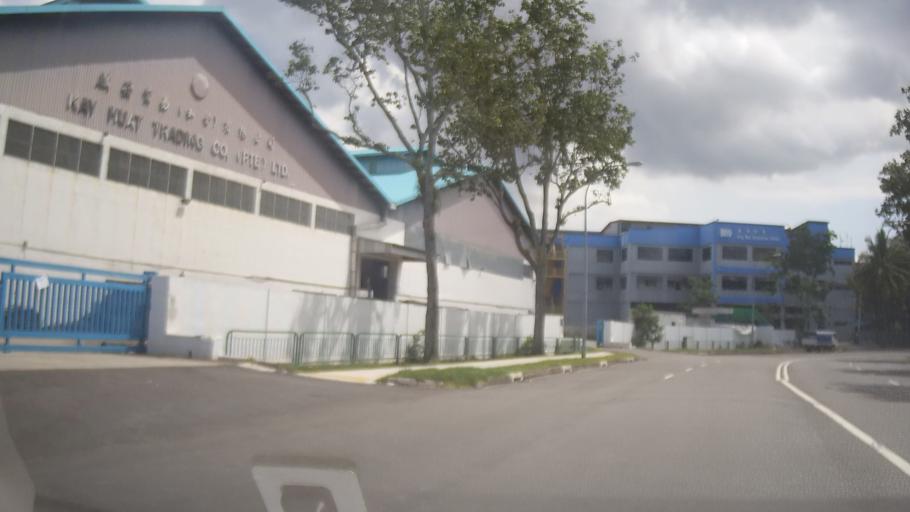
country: MY
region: Johor
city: Johor Bahru
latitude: 1.4192
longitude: 103.7418
